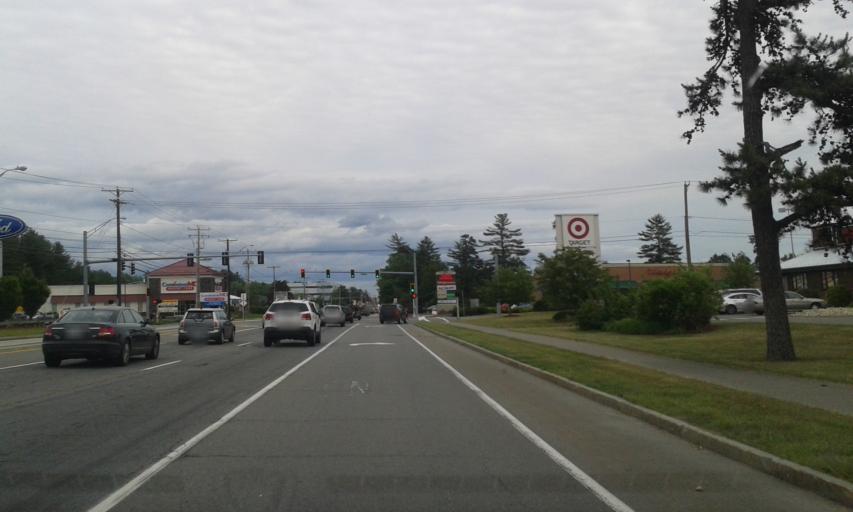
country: US
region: New Hampshire
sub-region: Hillsborough County
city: Litchfield
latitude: 42.7995
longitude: -71.5346
